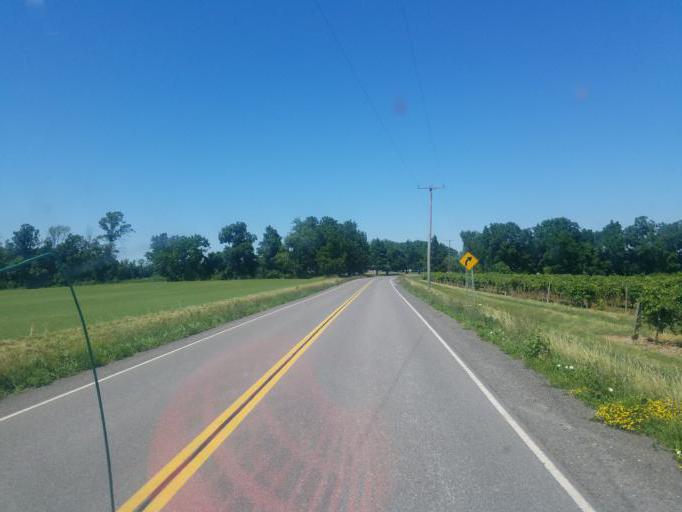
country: US
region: New York
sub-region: Yates County
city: Penn Yan
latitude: 42.7068
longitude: -76.9990
